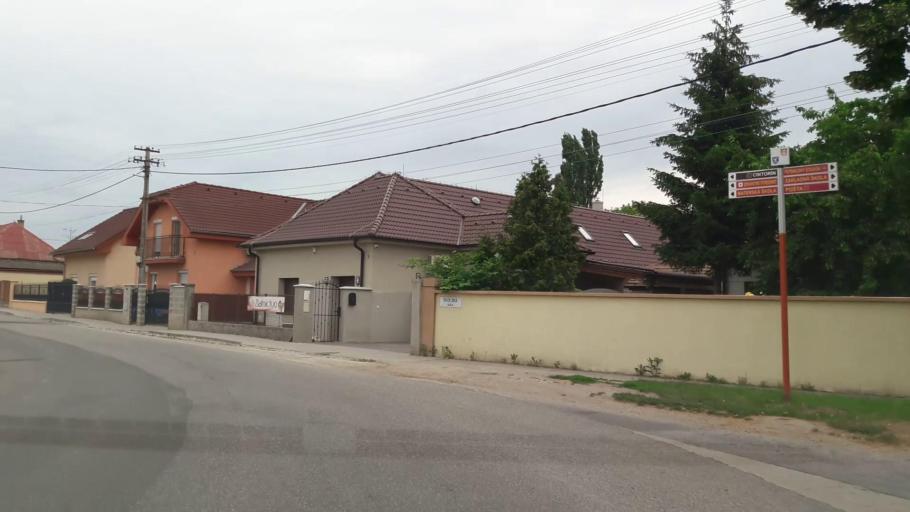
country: SK
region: Bratislavsky
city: Senec
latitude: 48.2143
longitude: 17.3605
